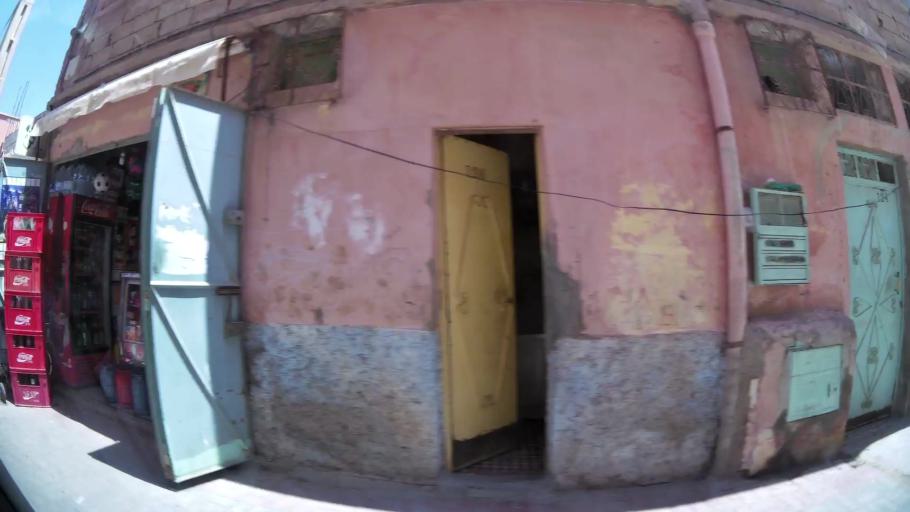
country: MA
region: Souss-Massa-Draa
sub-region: Inezgane-Ait Mellou
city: Inezgane
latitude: 30.3438
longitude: -9.4960
